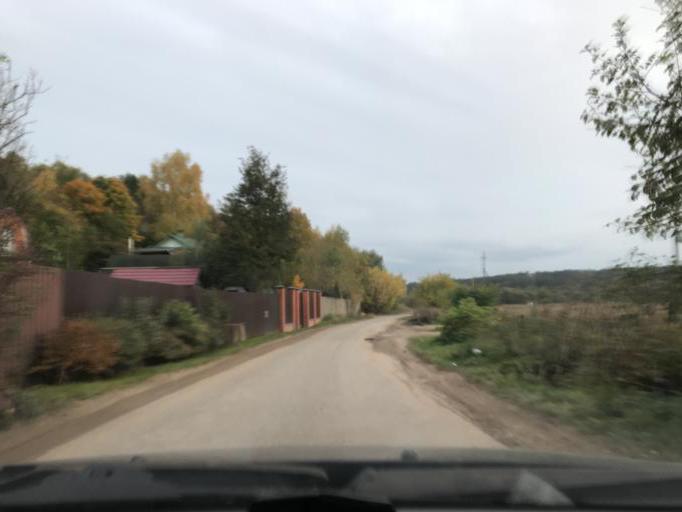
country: RU
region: Kaluga
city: Kaluga
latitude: 54.5480
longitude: 36.2308
